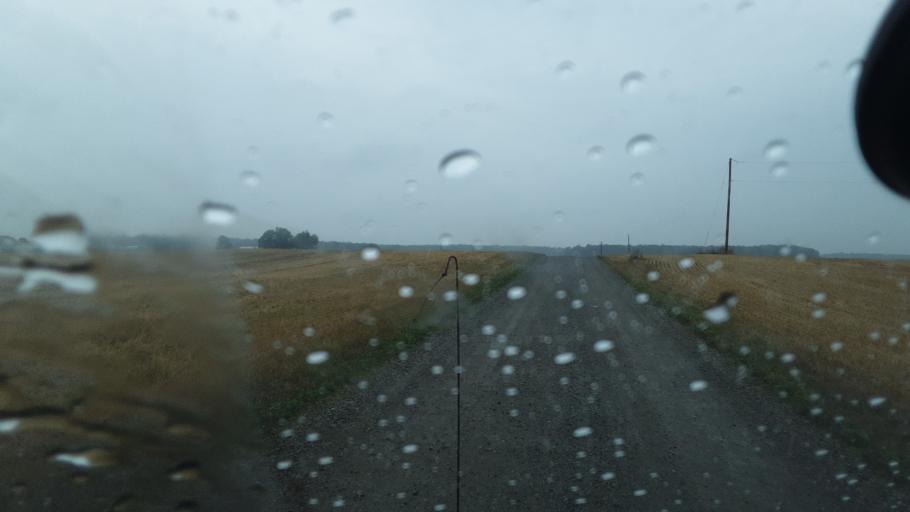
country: US
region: Indiana
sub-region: DeKalb County
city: Butler
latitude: 41.4151
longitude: -84.8130
